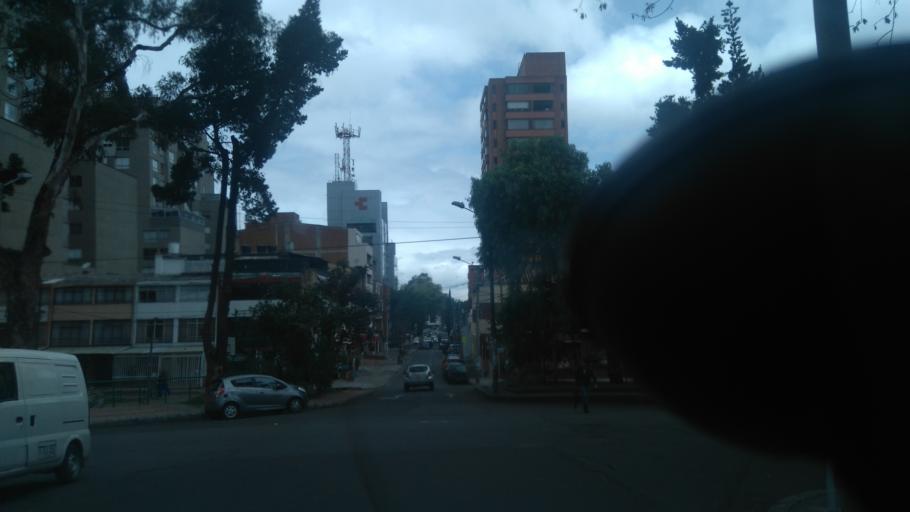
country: CO
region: Bogota D.C.
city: Bogota
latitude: 4.6296
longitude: -74.0656
